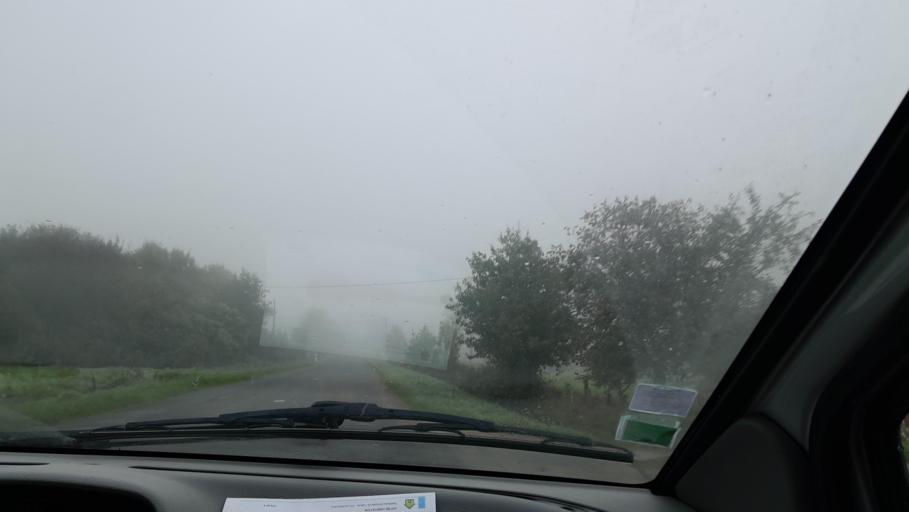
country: FR
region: Pays de la Loire
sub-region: Departement de la Mayenne
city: Saint-Pierre-la-Cour
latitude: 48.0885
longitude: -1.0179
